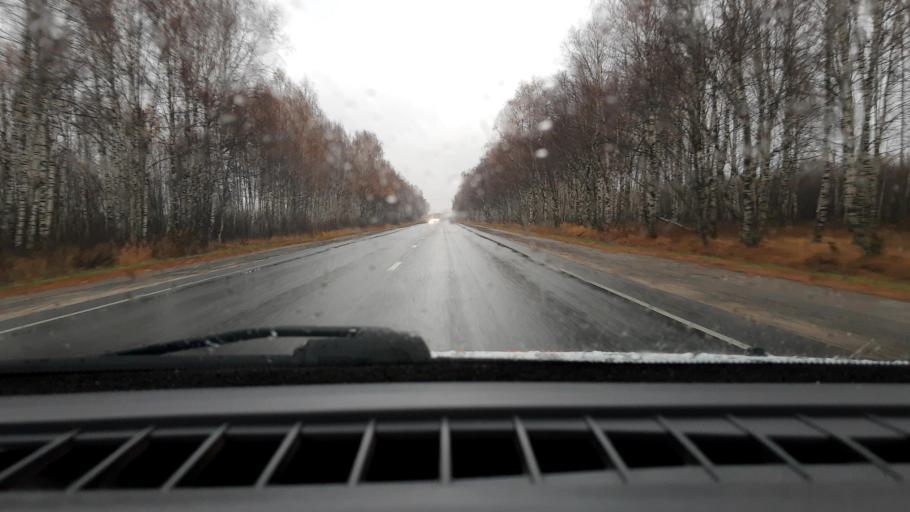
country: RU
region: Nizjnij Novgorod
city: Sitniki
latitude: 56.5174
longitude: 44.0250
